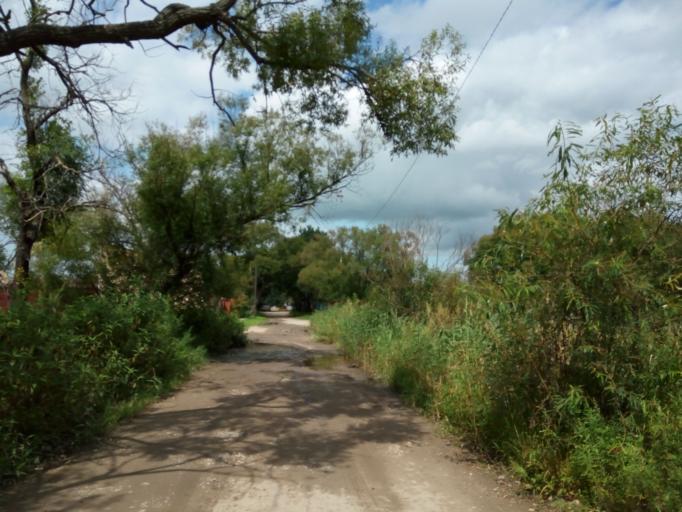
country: RU
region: Primorskiy
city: Dal'nerechensk
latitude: 45.9365
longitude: 133.8109
